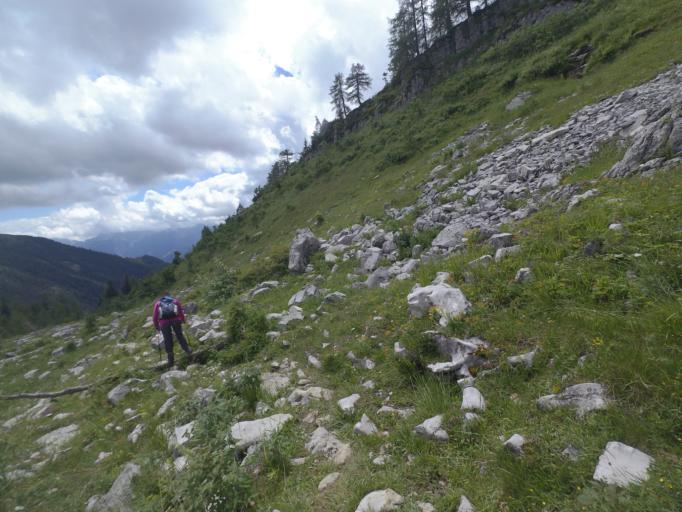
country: AT
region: Salzburg
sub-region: Politischer Bezirk Salzburg-Umgebung
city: Hintersee
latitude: 47.6628
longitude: 13.3014
